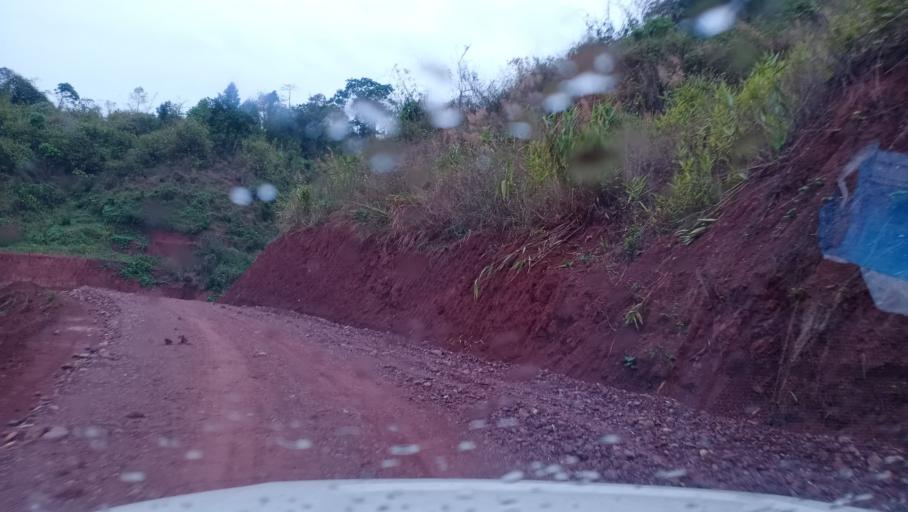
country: CN
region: Yunnan
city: Menglie
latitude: 22.2012
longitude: 101.6768
